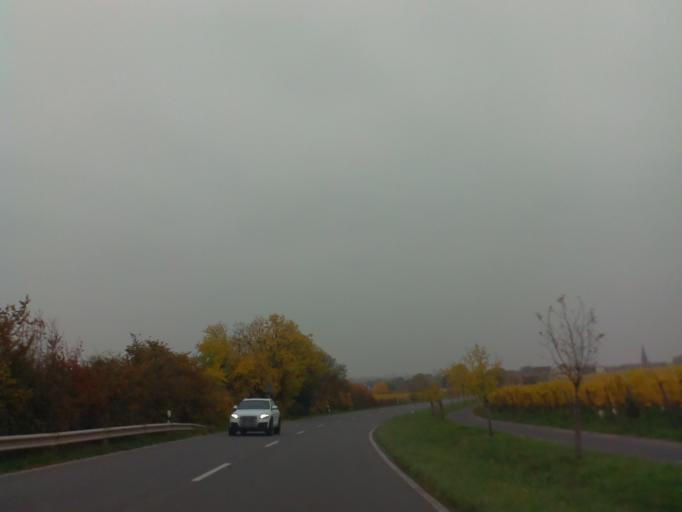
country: DE
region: Rheinland-Pfalz
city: Wachenheim
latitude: 49.4350
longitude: 8.1851
